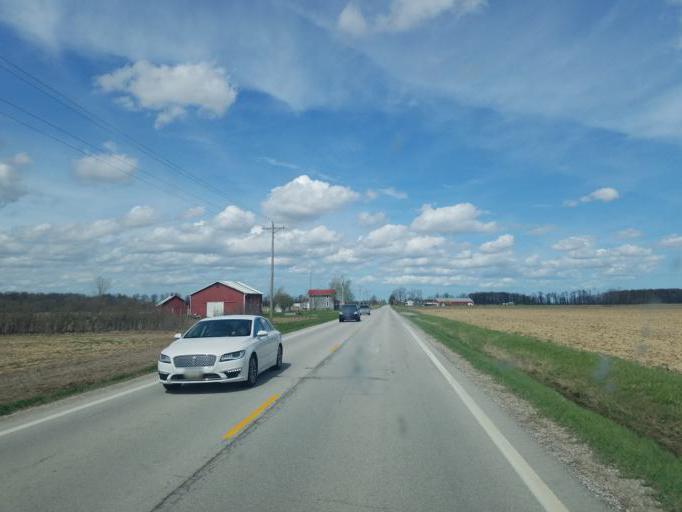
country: US
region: Ohio
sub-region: Huron County
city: Bellevue
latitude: 41.2058
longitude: -82.8220
